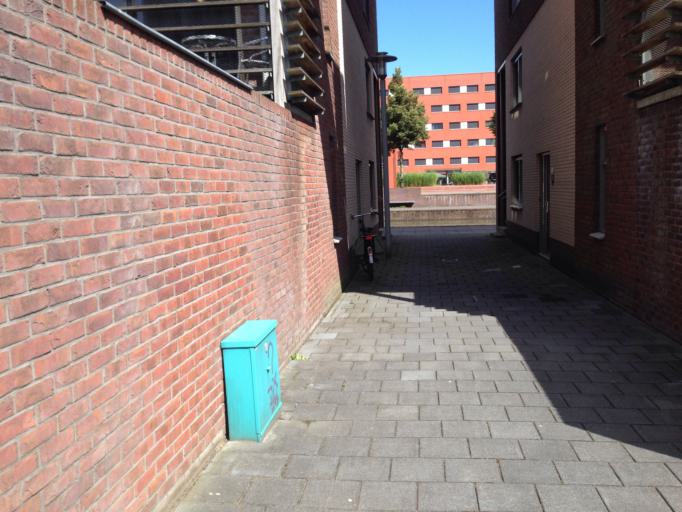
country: NL
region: Overijssel
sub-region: Gemeente Zwolle
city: Zwolle
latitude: 52.5023
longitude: 6.0900
